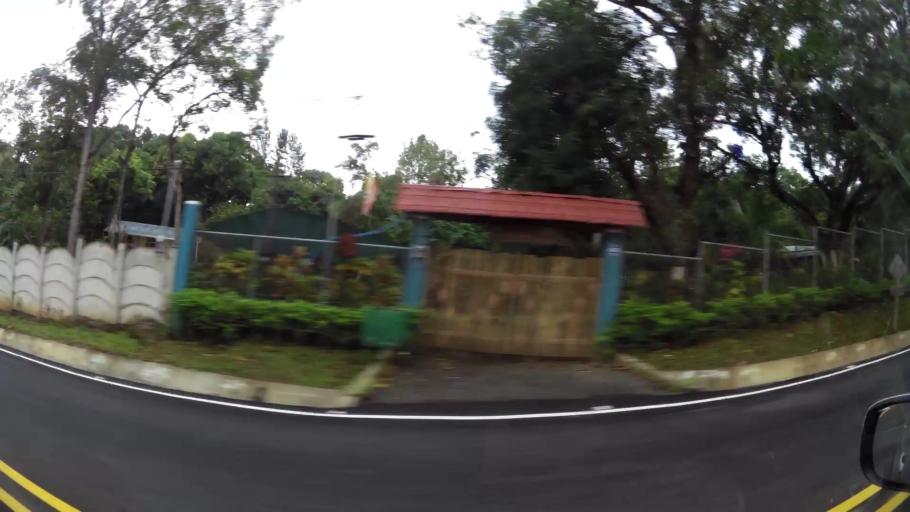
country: CR
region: Alajuela
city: Desamparados
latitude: 9.9382
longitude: -84.5314
